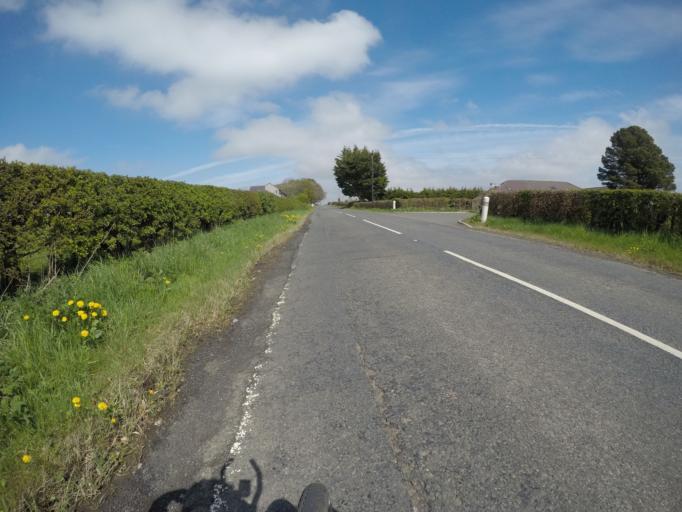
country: GB
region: Scotland
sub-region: East Ayrshire
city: Stewarton
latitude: 55.6977
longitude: -4.4865
